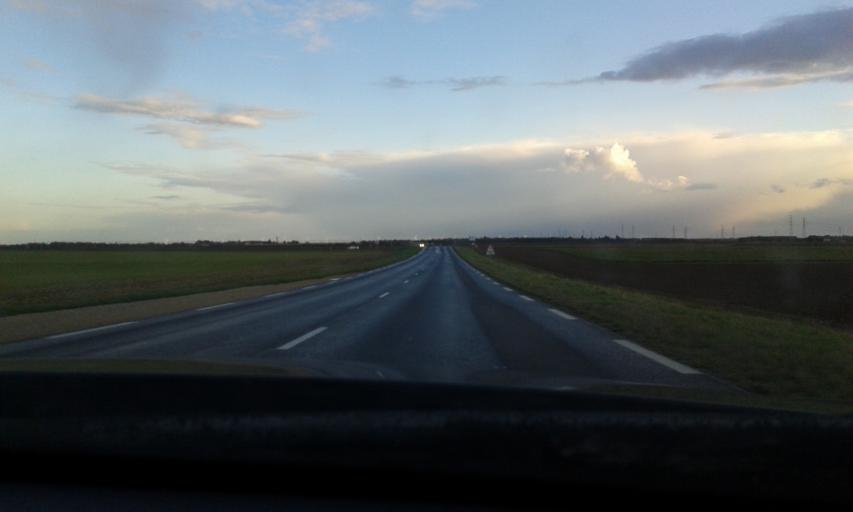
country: FR
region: Centre
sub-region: Departement d'Eure-et-Loir
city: Janville
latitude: 48.2407
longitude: 1.7798
